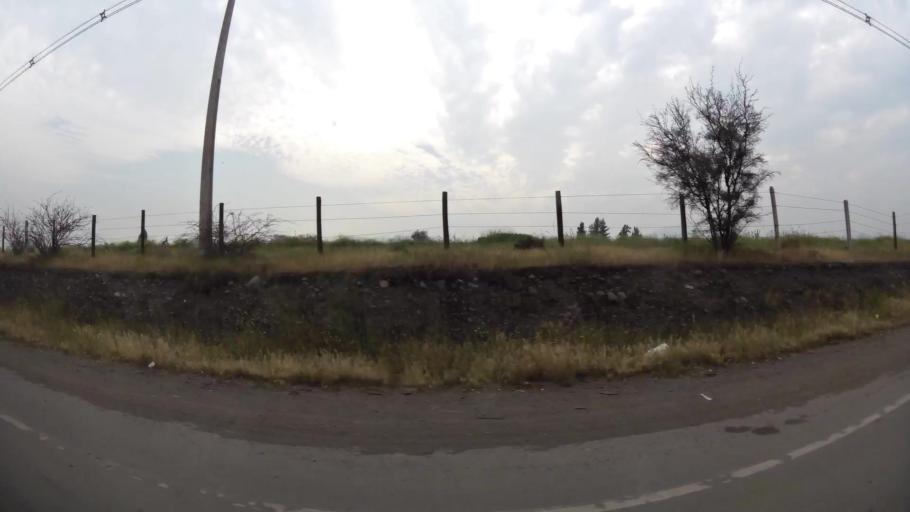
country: CL
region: Santiago Metropolitan
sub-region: Provincia de Chacabuco
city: Chicureo Abajo
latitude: -33.2103
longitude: -70.6701
